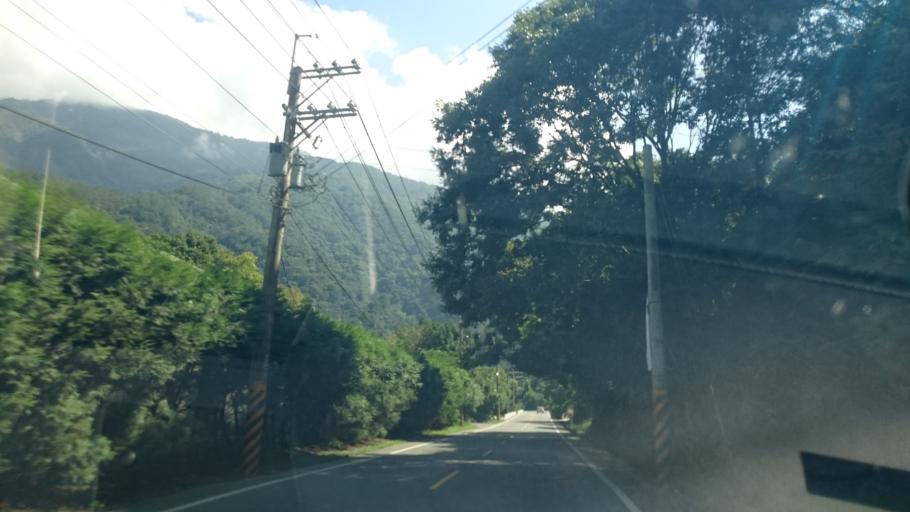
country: TW
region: Taiwan
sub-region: Nantou
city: Puli
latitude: 23.9991
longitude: 121.0514
